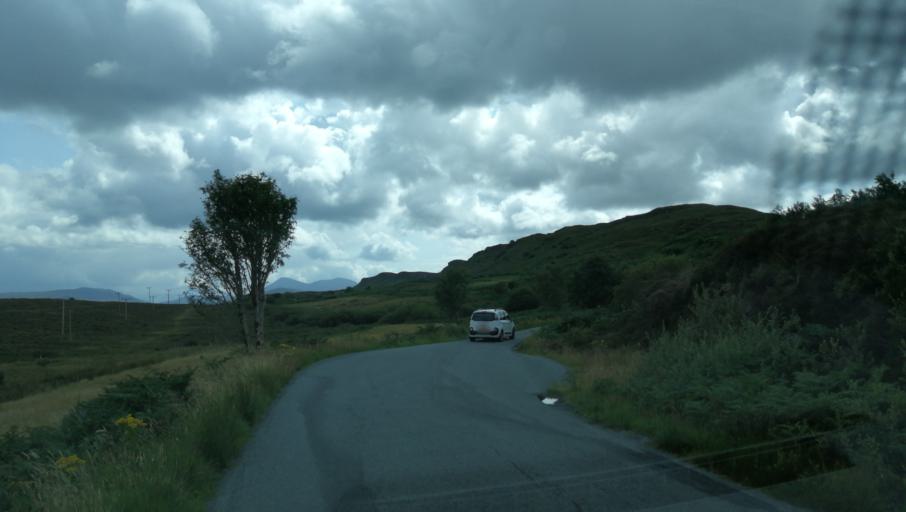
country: GB
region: Scotland
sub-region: Highland
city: Portree
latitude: 57.3796
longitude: -6.1701
